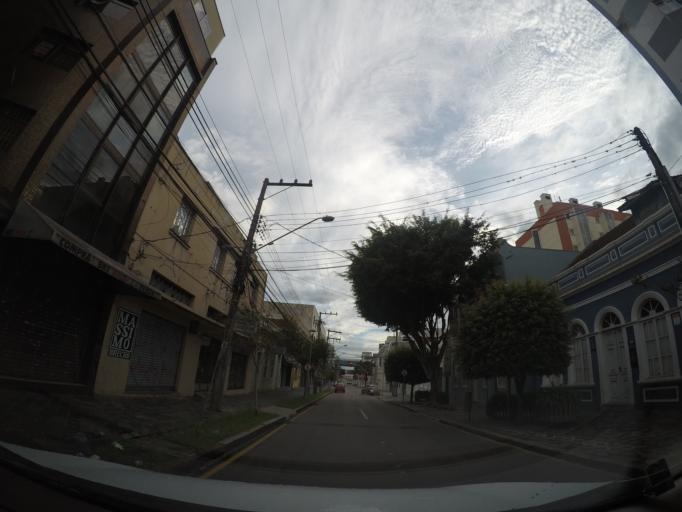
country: BR
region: Parana
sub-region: Curitiba
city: Curitiba
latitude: -25.4249
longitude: -49.2714
